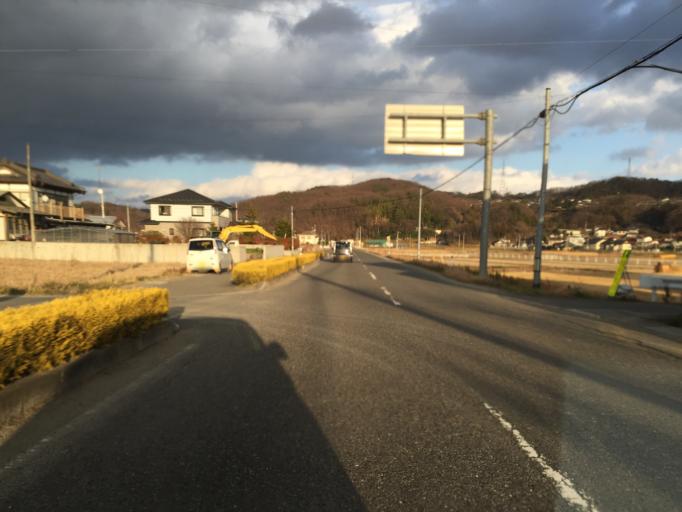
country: JP
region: Fukushima
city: Motomiya
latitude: 37.5177
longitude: 140.4105
